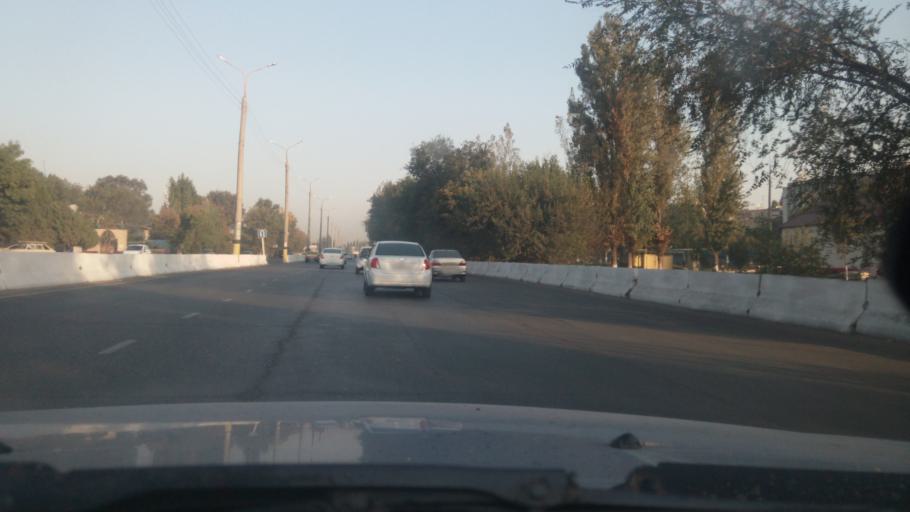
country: UZ
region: Toshkent Shahri
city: Tashkent
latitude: 41.2566
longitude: 69.1547
